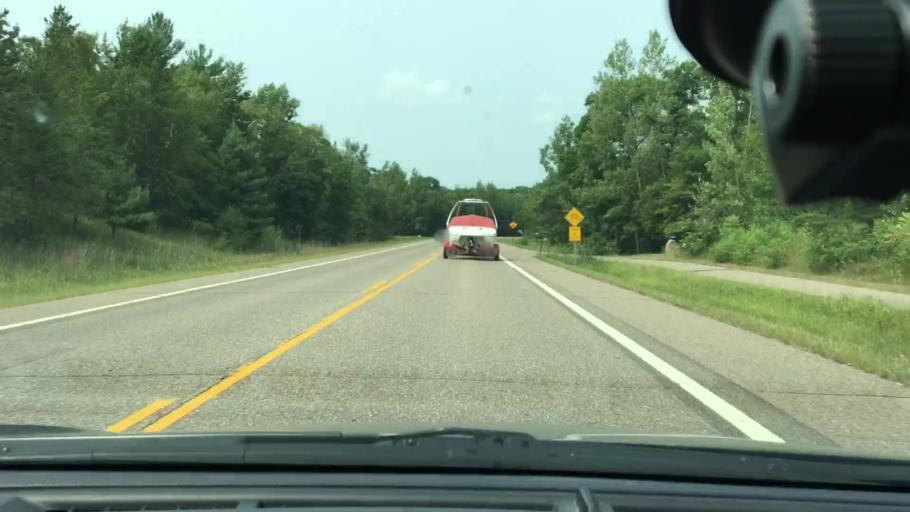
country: US
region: Minnesota
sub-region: Cass County
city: East Gull Lake
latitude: 46.4054
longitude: -94.3537
